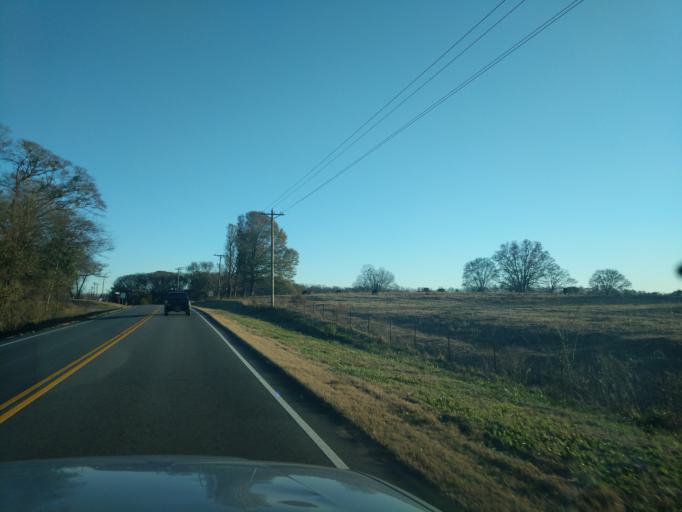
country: US
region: South Carolina
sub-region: Oconee County
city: Utica
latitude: 34.5696
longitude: -82.9075
